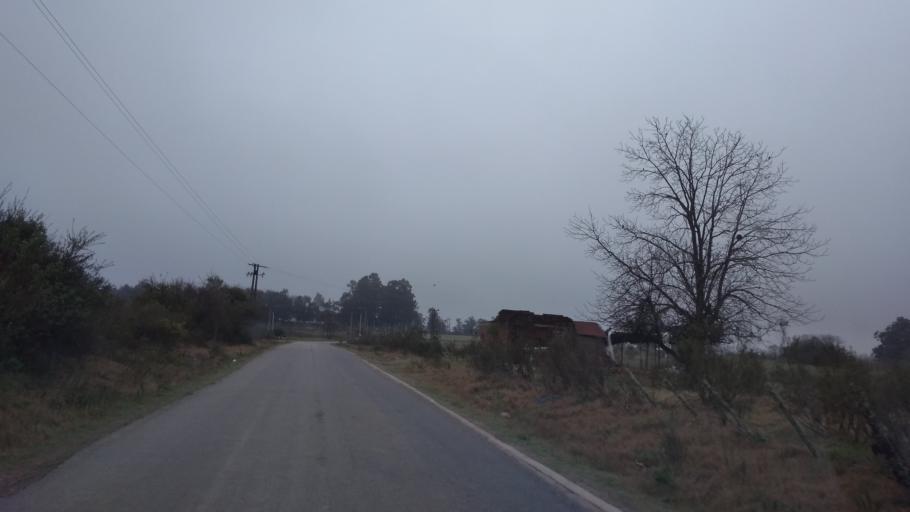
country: UY
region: Florida
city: Florida
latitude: -34.0829
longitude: -56.2051
